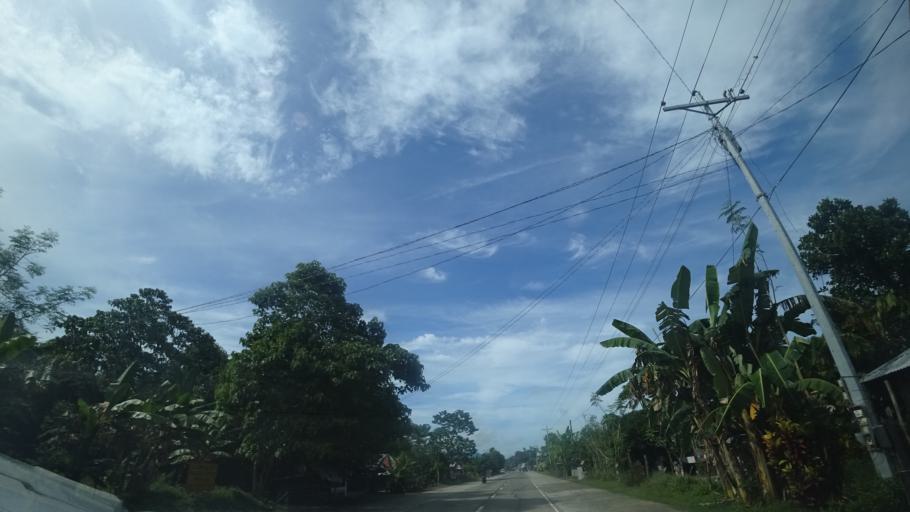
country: PH
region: Eastern Visayas
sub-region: Province of Leyte
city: Liberty
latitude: 10.8601
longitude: 124.9944
